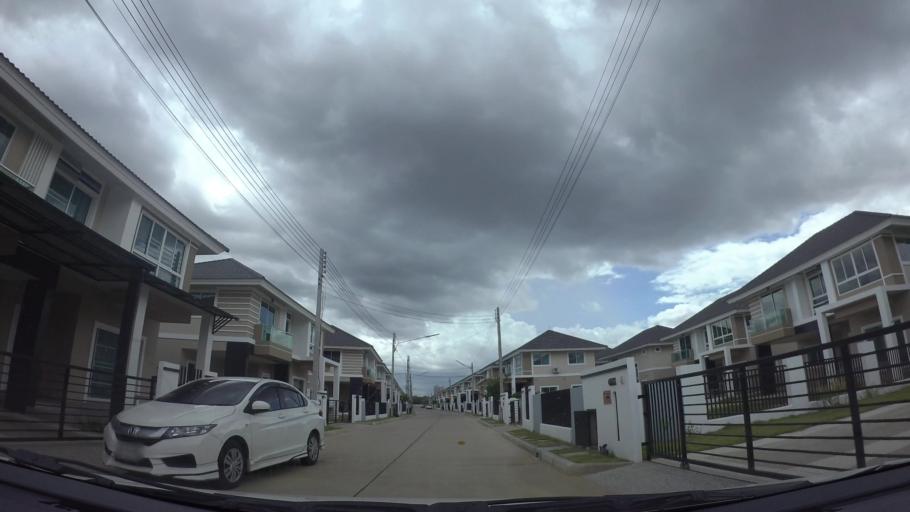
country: TH
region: Chiang Mai
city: Saraphi
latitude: 18.7496
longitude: 99.0464
